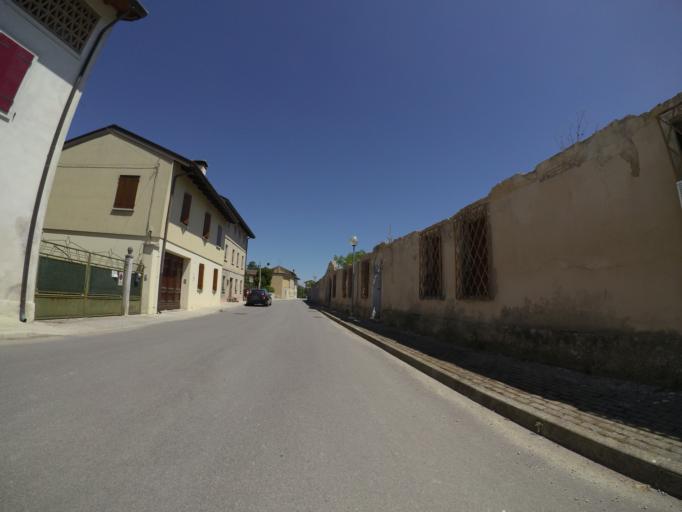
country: IT
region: Friuli Venezia Giulia
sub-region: Provincia di Udine
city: Teor
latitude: 45.8491
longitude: 13.0406
